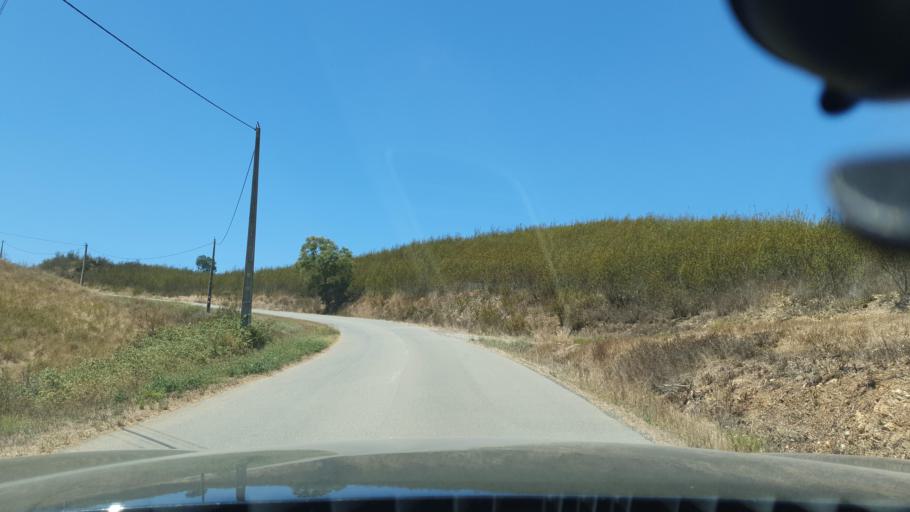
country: PT
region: Beja
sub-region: Ourique
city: Ourique
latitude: 37.5552
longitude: -8.4060
